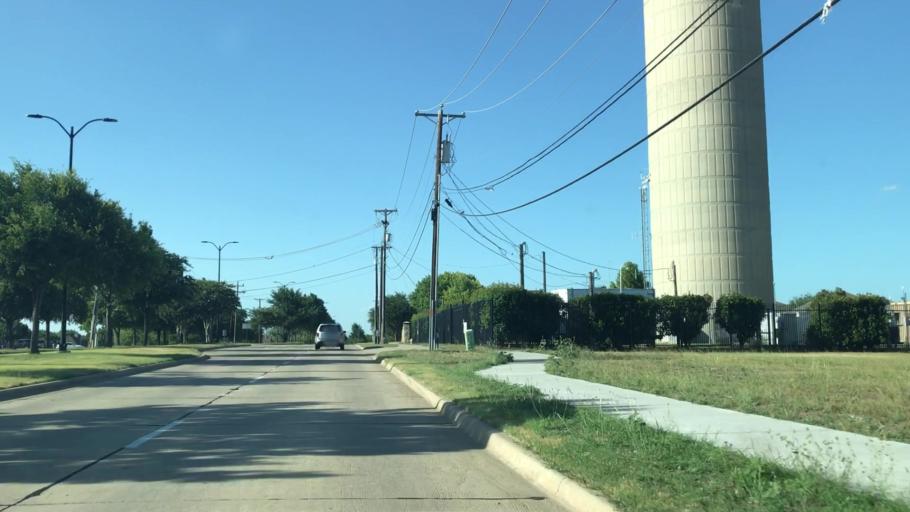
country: US
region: Texas
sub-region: Collin County
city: Frisco
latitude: 33.1321
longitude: -96.7867
